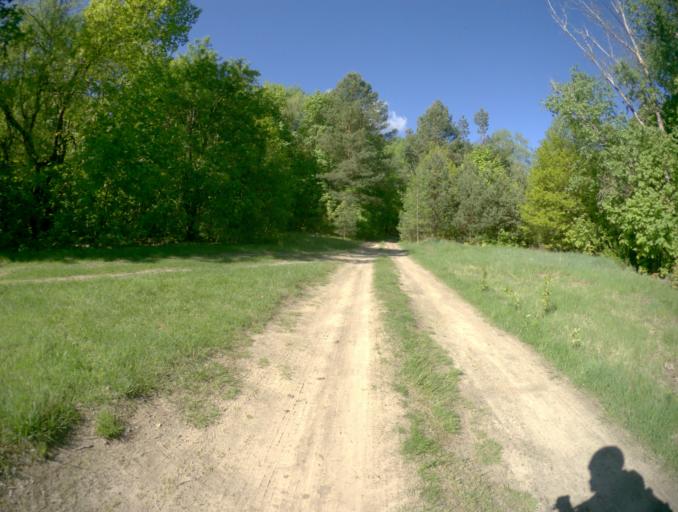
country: RU
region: Rjazan
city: Spas-Klepiki
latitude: 55.2535
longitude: 40.1121
